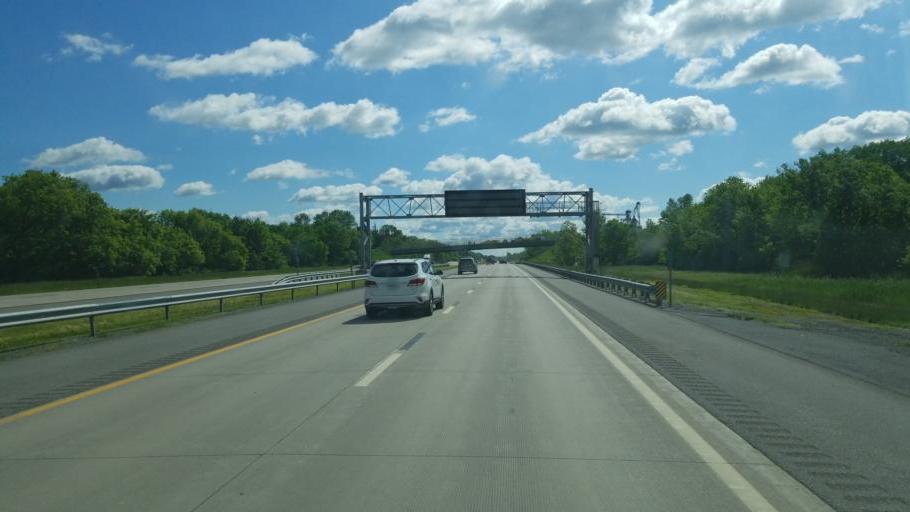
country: US
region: New York
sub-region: Onondaga County
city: Jordan
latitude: 43.0764
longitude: -76.4848
